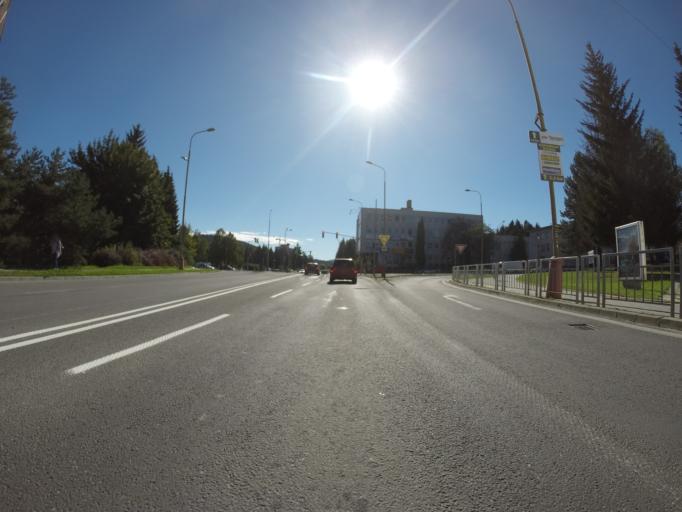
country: SK
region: Trenciansky
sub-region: Okres Povazska Bystrica
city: Povazska Bystrica
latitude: 49.1164
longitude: 18.4413
